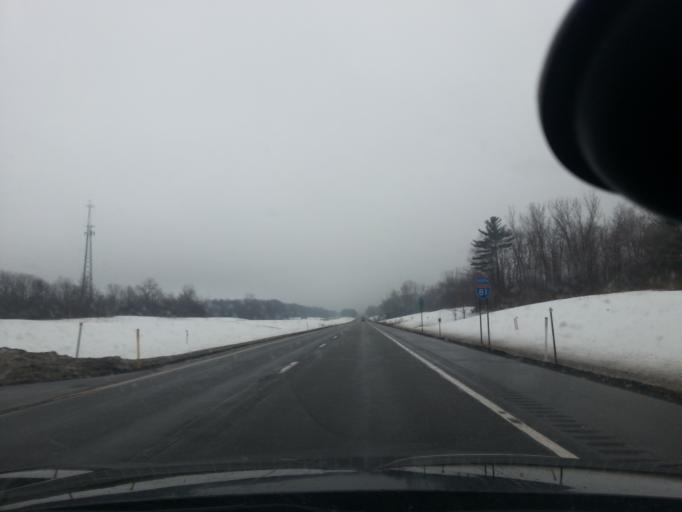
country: US
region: New York
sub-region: Jefferson County
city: Adams
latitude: 43.7098
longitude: -76.0760
